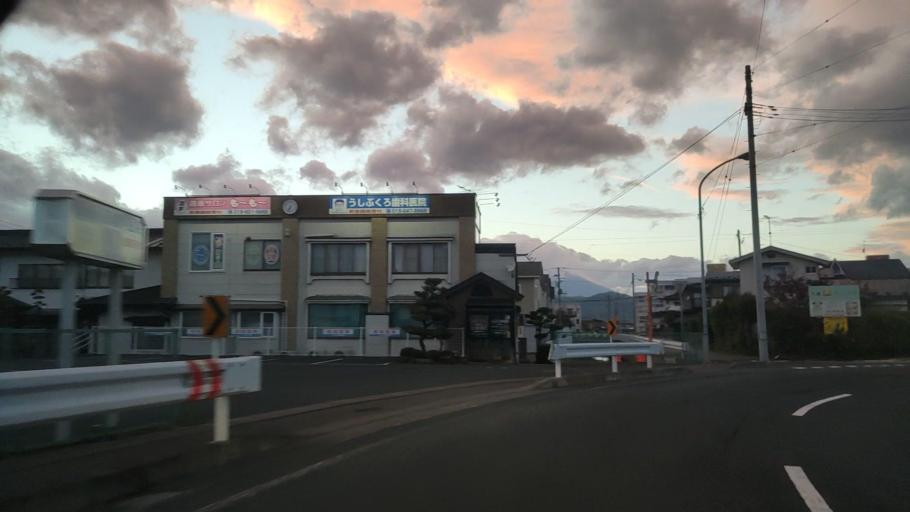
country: JP
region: Iwate
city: Morioka-shi
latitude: 39.7189
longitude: 141.1084
